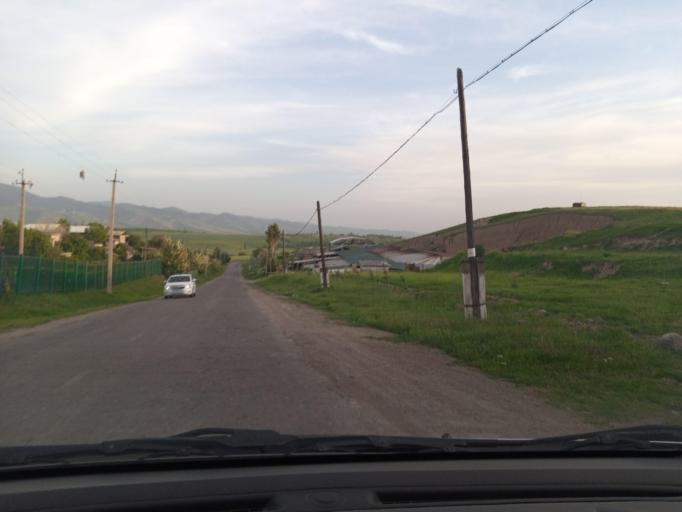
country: UZ
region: Toshkent
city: Parkent
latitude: 41.2339
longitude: 69.7374
